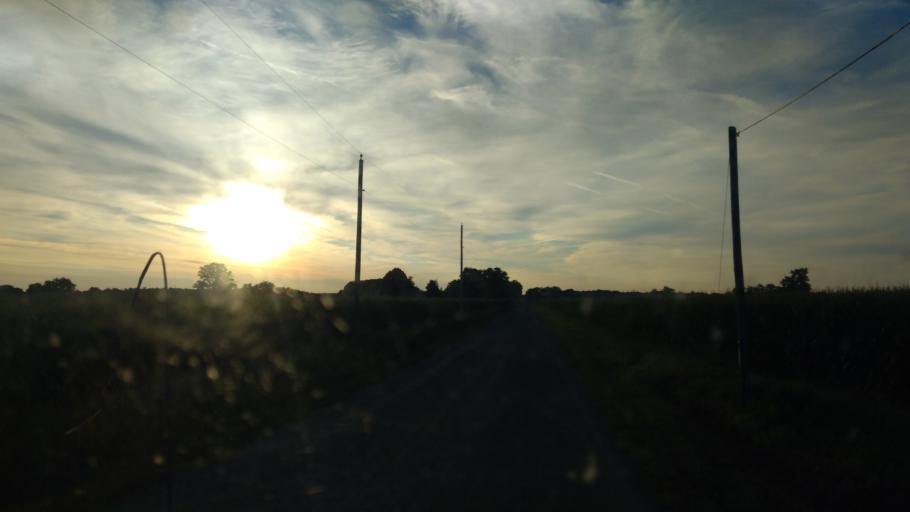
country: US
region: Indiana
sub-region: Adams County
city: Berne
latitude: 40.6417
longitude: -85.0194
